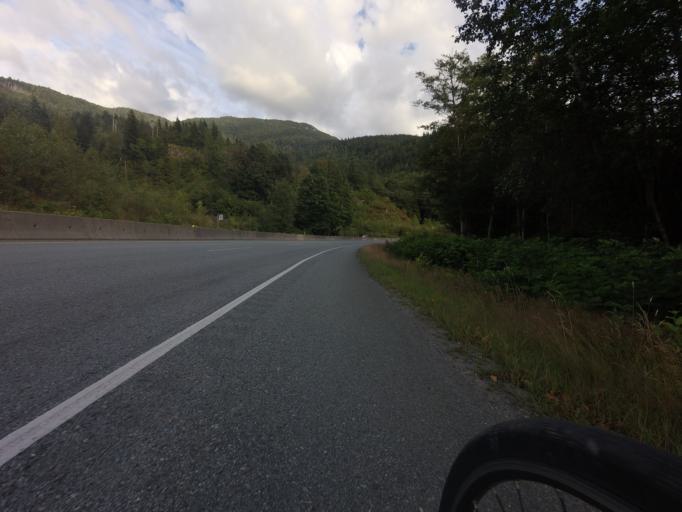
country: CA
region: British Columbia
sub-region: Greater Vancouver Regional District
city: Lions Bay
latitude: 49.6107
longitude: -123.2077
